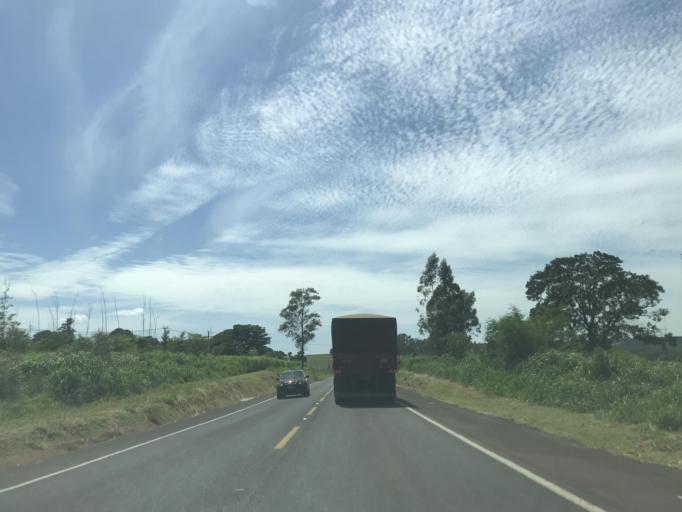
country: BR
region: Parana
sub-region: Paranavai
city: Nova Aurora
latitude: -22.9568
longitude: -52.6675
